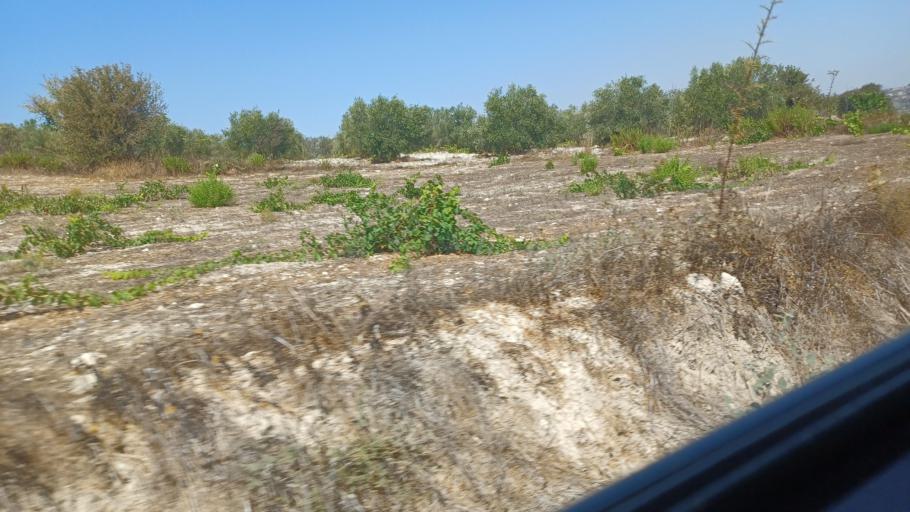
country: CY
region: Pafos
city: Tala
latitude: 34.8607
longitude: 32.4720
